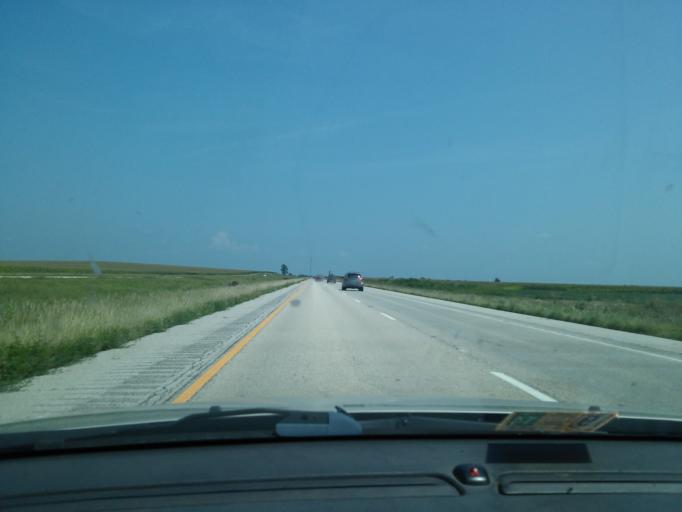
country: US
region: Illinois
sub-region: Morgan County
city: Jacksonville
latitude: 39.7382
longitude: -90.1045
